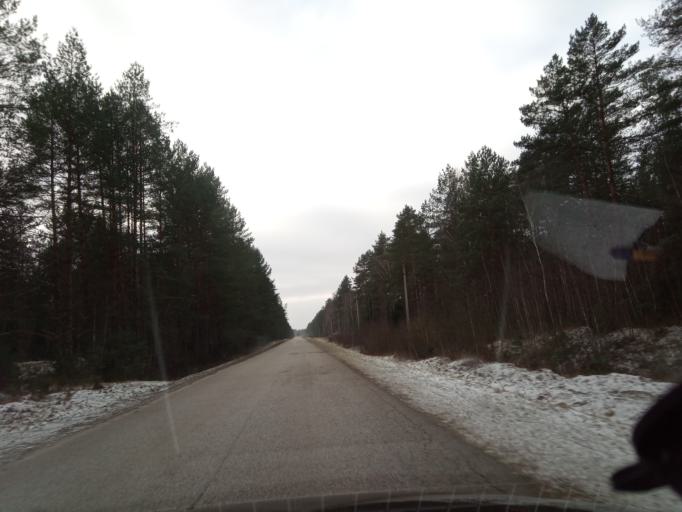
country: LT
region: Alytaus apskritis
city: Varena
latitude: 54.0331
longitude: 24.3635
